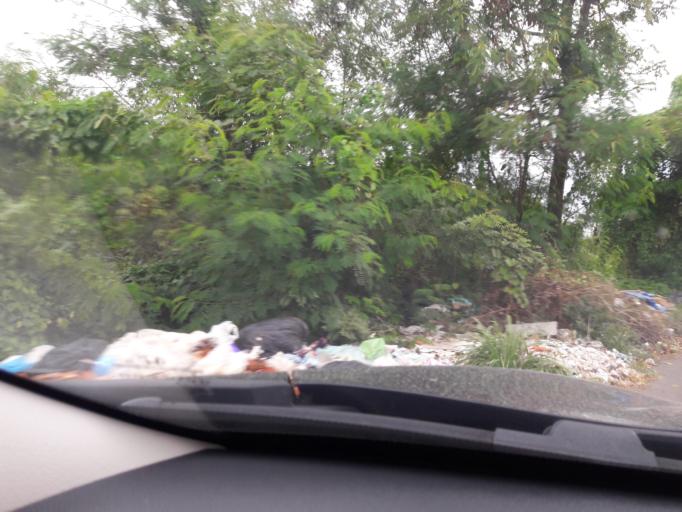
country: TH
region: Ratchaburi
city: Damnoen Saduak
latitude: 13.5930
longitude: 99.9457
